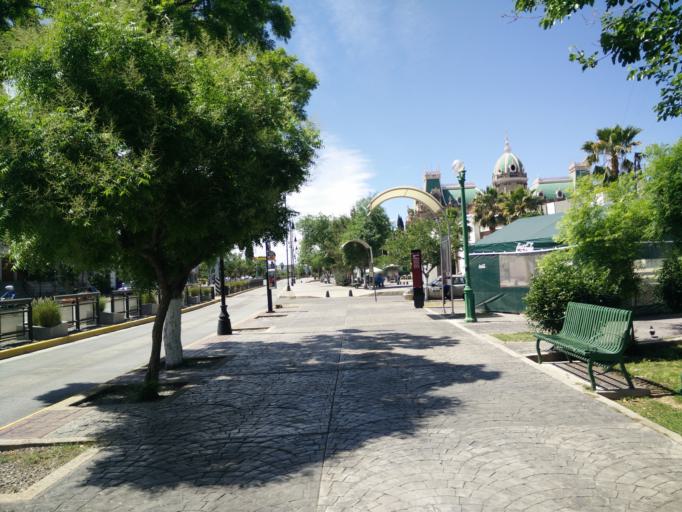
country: MX
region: Chihuahua
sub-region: Chihuahua
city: Chihuahua
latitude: 28.6332
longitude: -106.0729
